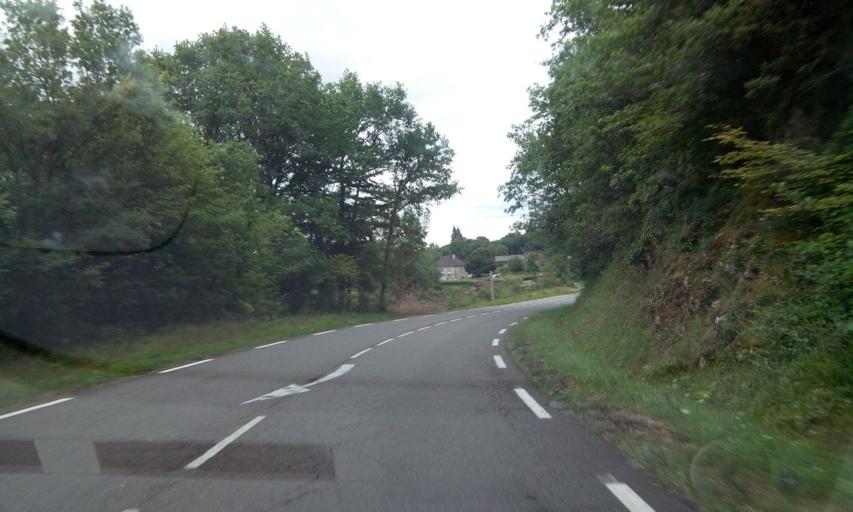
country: FR
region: Limousin
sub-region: Departement de la Correze
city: Cosnac
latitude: 45.0648
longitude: 1.5632
